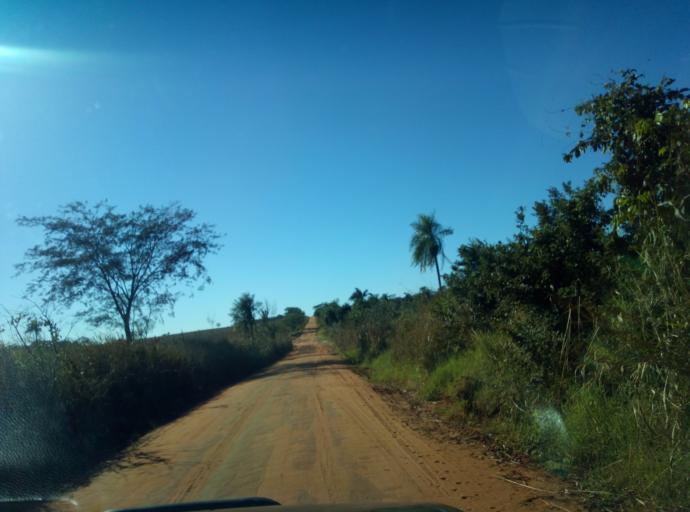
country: PY
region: Caaguazu
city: Doctor Cecilio Baez
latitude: -25.1606
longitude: -56.2794
